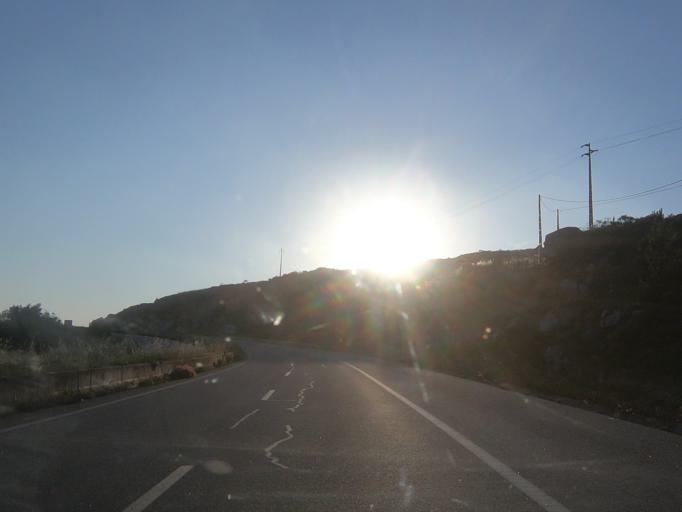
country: PT
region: Guarda
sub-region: Celorico da Beira
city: Celorico da Beira
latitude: 40.6346
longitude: -7.4447
